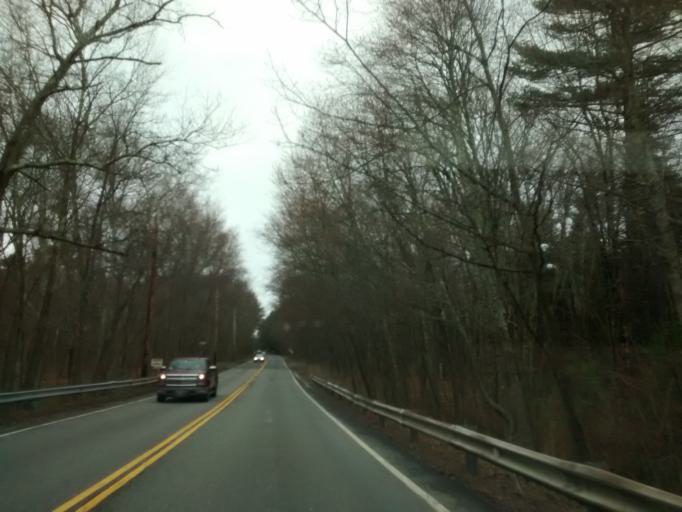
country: US
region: Massachusetts
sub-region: Worcester County
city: Upton
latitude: 42.1958
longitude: -71.5771
